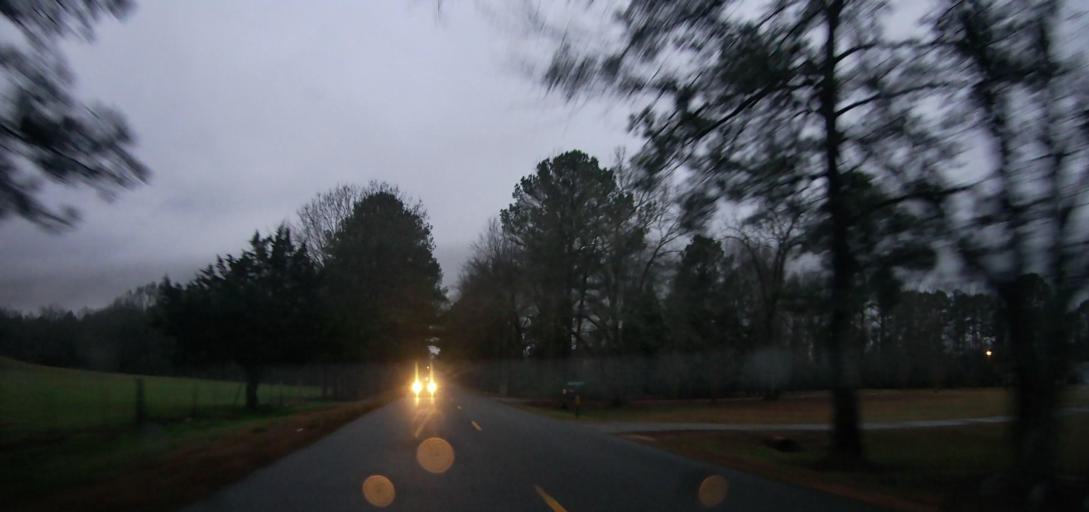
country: US
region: Alabama
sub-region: Tuscaloosa County
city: Vance
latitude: 33.1397
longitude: -87.2297
